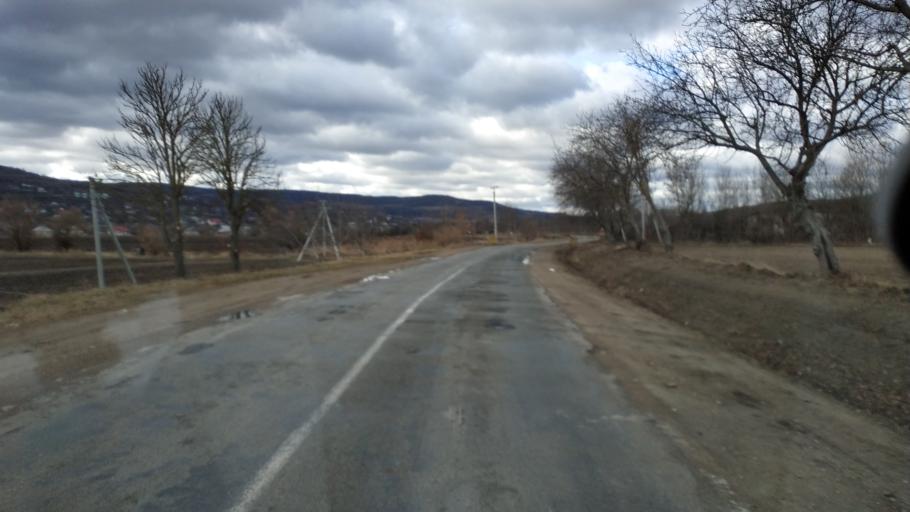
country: MD
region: Stinga Nistrului
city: Bucovat
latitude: 47.1681
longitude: 28.4403
